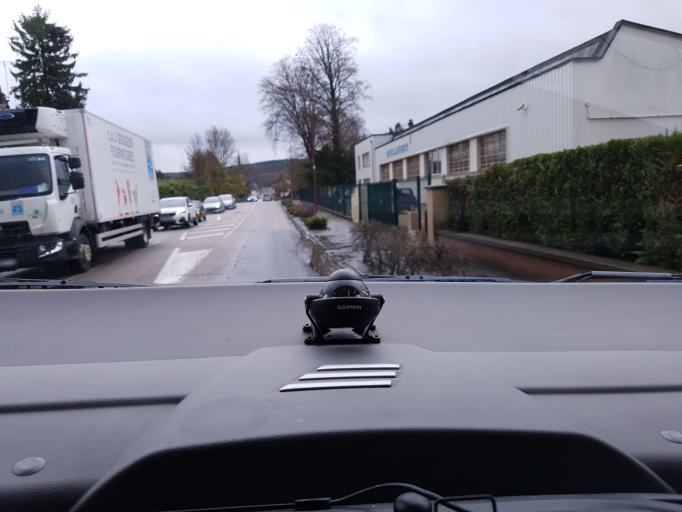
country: FR
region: Haute-Normandie
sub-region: Departement de l'Eure
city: Pont-Saint-Pierre
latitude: 49.3360
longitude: 1.2691
